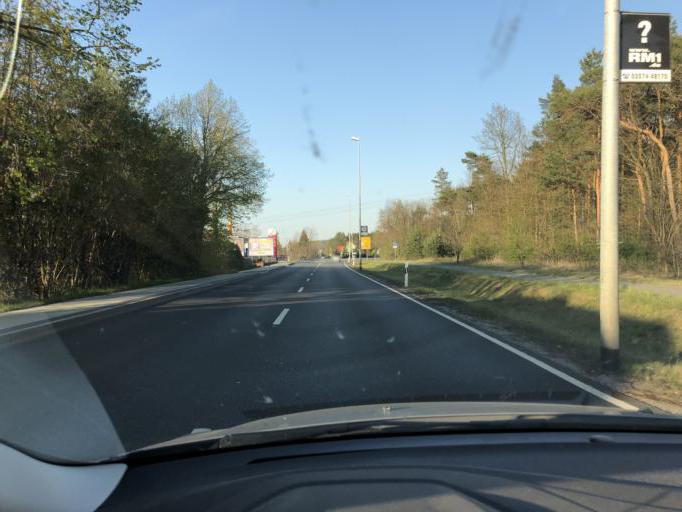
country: DE
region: Brandenburg
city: Ruhland
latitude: 51.4753
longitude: 13.8984
